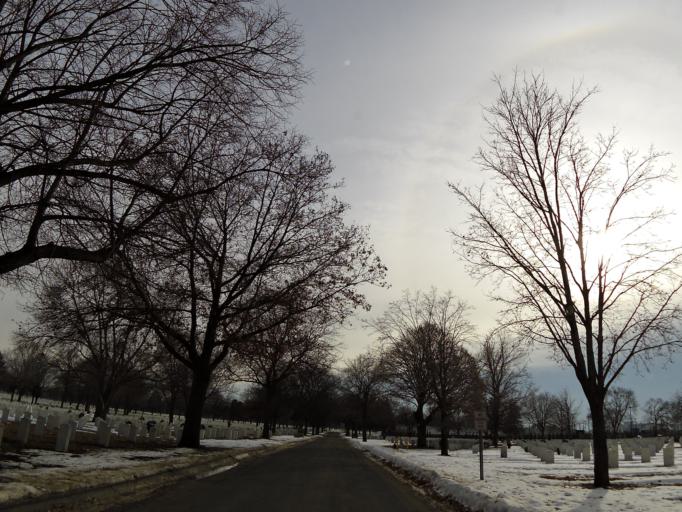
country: US
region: Minnesota
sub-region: Hennepin County
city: Richfield
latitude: 44.8748
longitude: -93.2221
